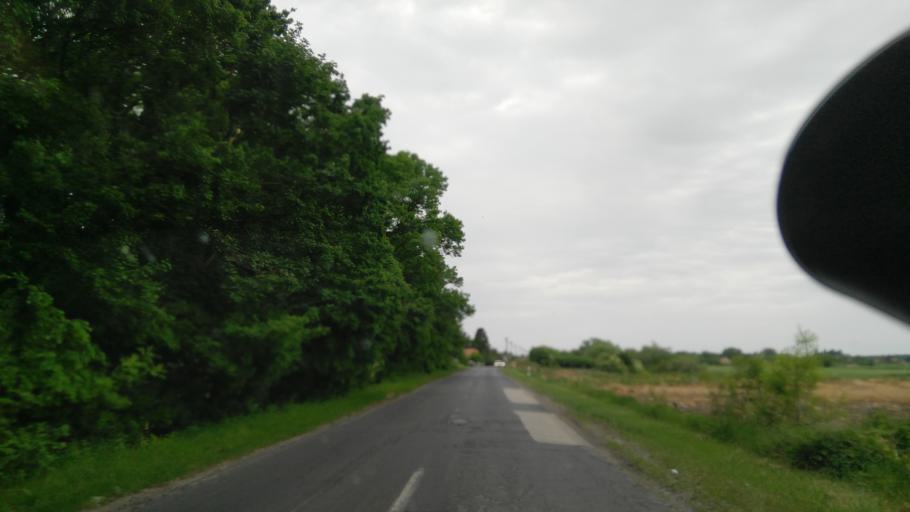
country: HU
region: Bekes
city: Doboz
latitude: 46.7329
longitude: 21.2611
